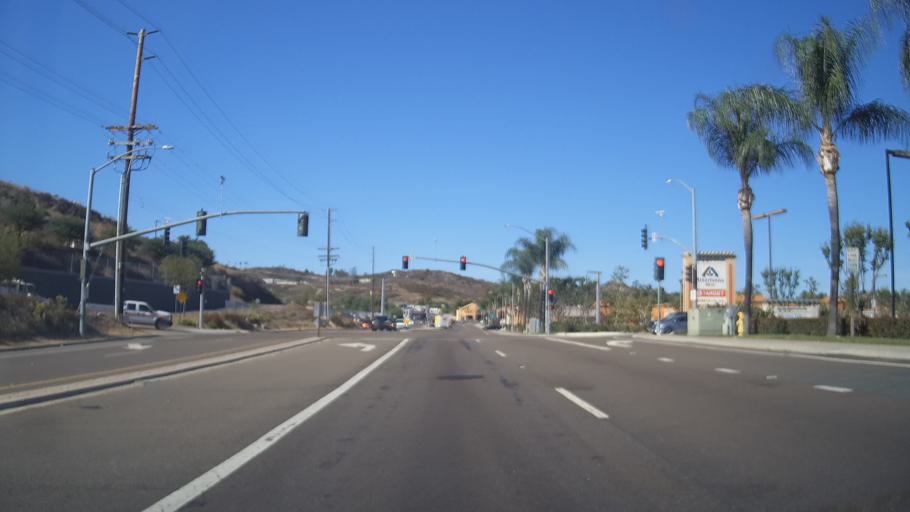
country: US
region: California
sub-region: San Diego County
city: Rancho San Diego
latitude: 32.7364
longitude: -116.9410
